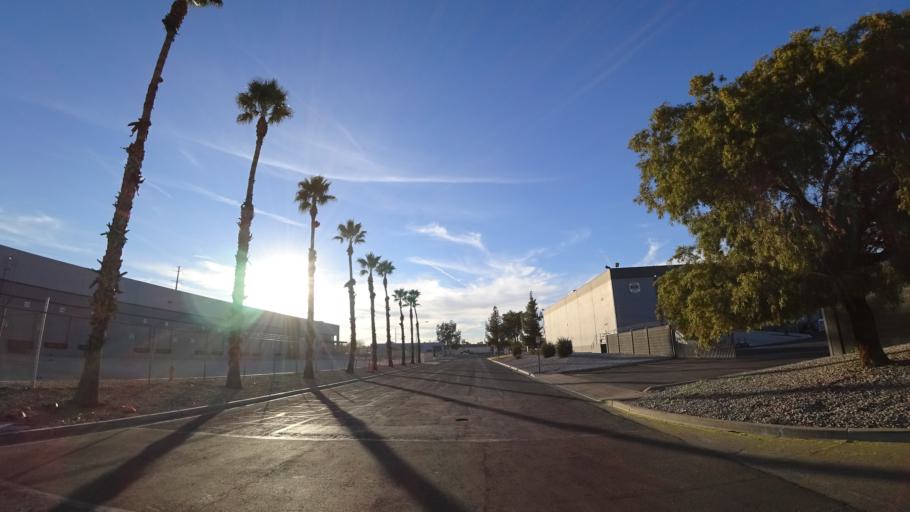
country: US
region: Arizona
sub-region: Maricopa County
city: Phoenix
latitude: 33.4234
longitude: -112.0671
